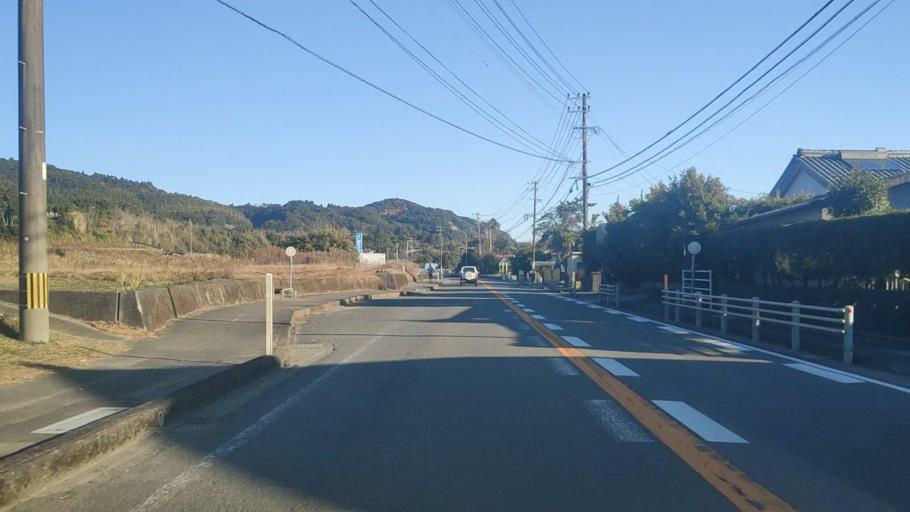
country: JP
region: Miyazaki
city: Nobeoka
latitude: 32.3609
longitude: 131.6222
